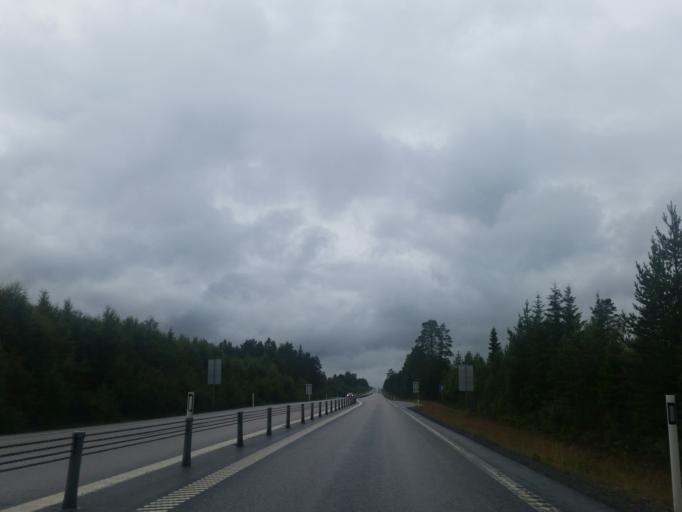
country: SE
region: Vaesterbotten
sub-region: Umea Kommun
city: Saevar
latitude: 63.9498
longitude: 20.6628
